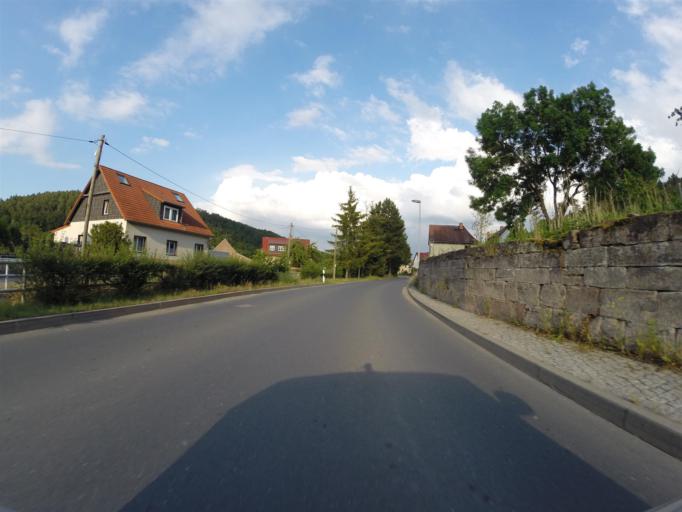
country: DE
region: Thuringia
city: Schops
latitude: 50.8377
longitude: 11.5771
